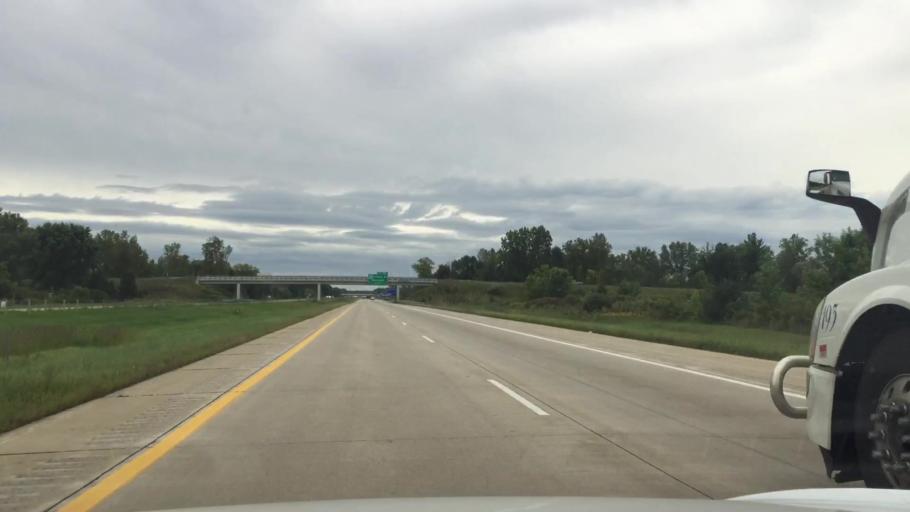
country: US
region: Michigan
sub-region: Saint Clair County
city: Marysville
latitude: 42.9374
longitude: -82.5070
